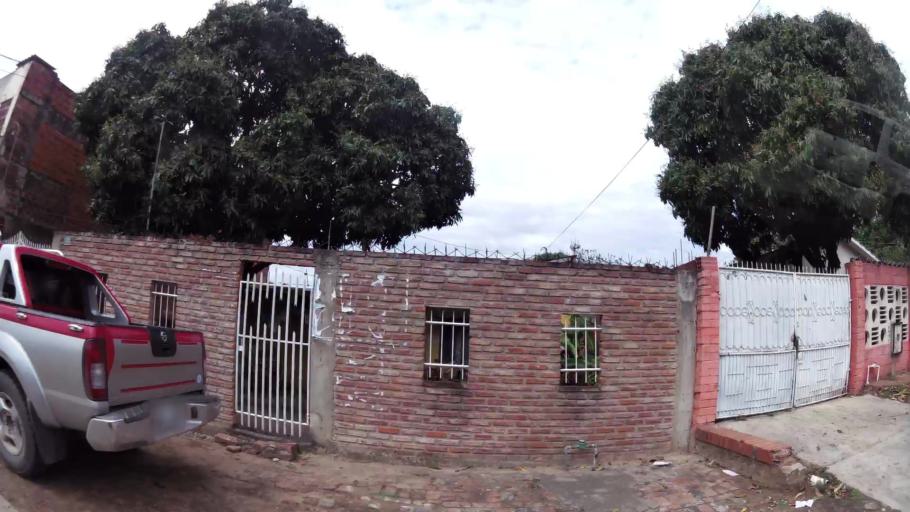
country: BO
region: Santa Cruz
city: Santa Cruz de la Sierra
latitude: -17.7489
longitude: -63.1910
